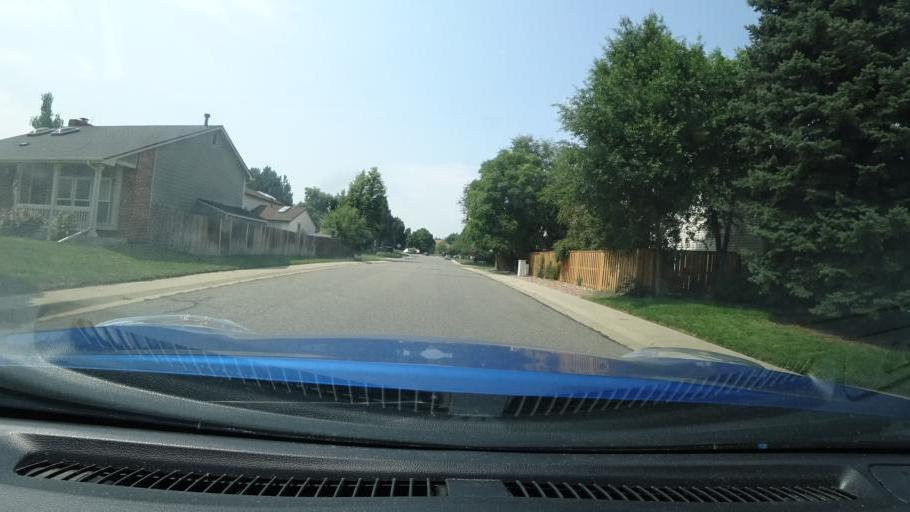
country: US
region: Colorado
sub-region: Adams County
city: Aurora
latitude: 39.7780
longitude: -104.7636
